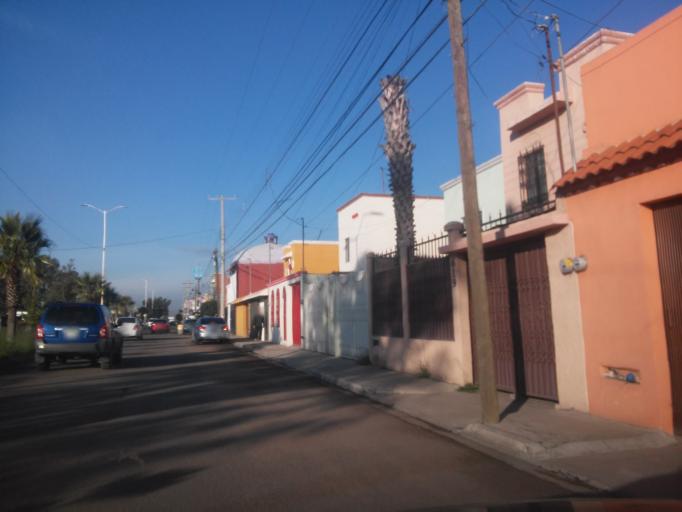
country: MX
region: Durango
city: Victoria de Durango
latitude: 24.0483
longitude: -104.6138
